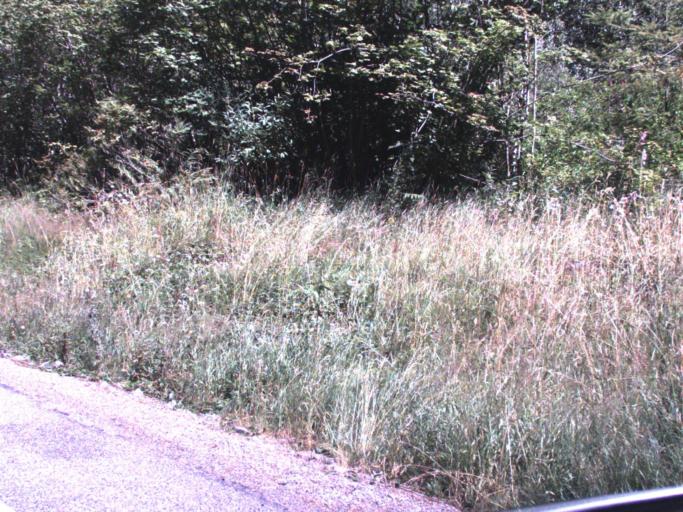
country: US
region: Washington
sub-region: King County
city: Enumclaw
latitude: 47.1755
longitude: -121.7809
